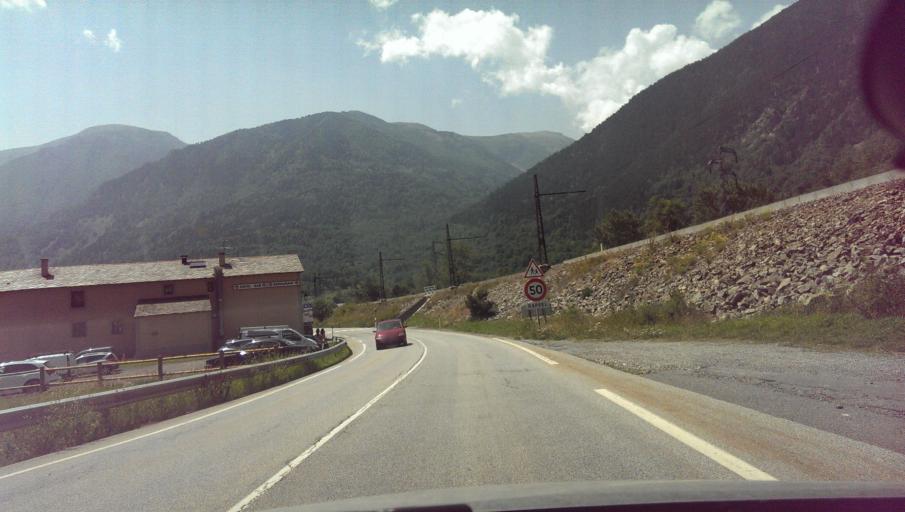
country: ES
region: Catalonia
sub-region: Provincia de Girona
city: Meranges
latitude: 42.5271
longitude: 1.8238
